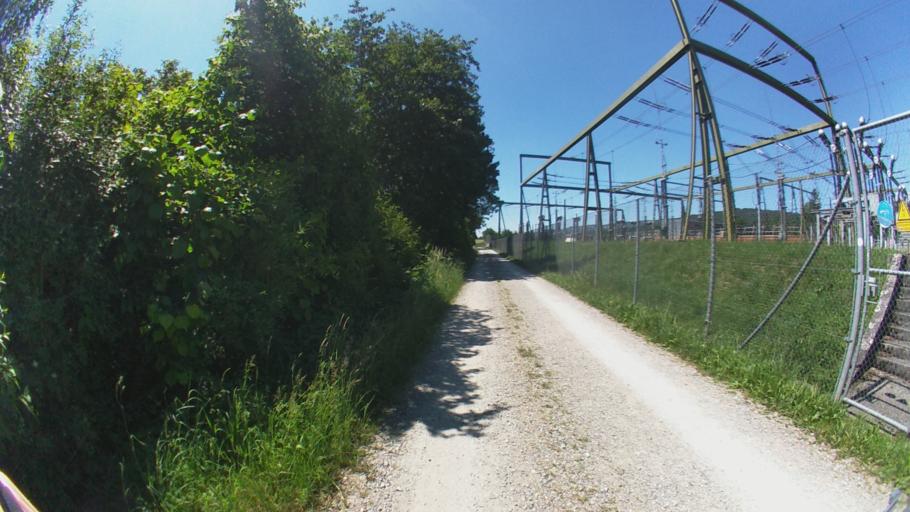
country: CH
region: Zurich
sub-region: Bezirk Dielsdorf
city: Sonnhalde
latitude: 47.4523
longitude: 8.4517
